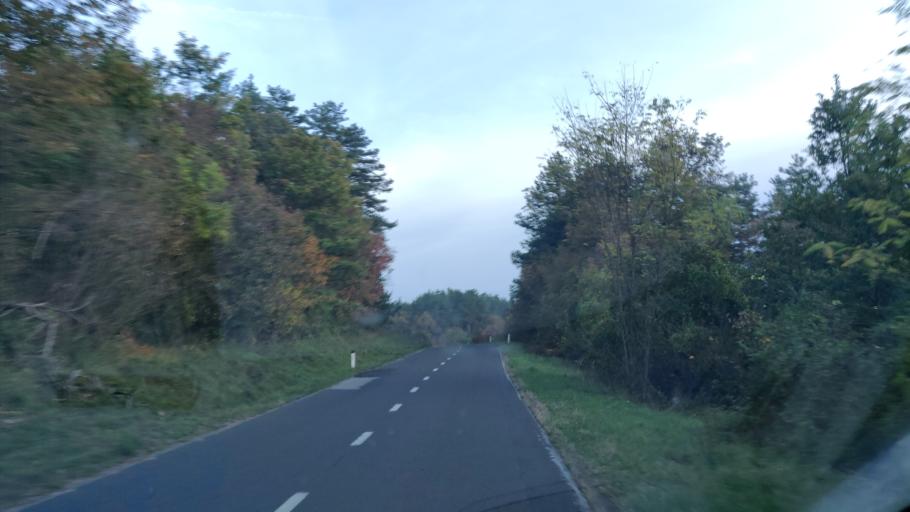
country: SI
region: Sezana
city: Sezana
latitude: 45.7720
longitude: 13.8774
